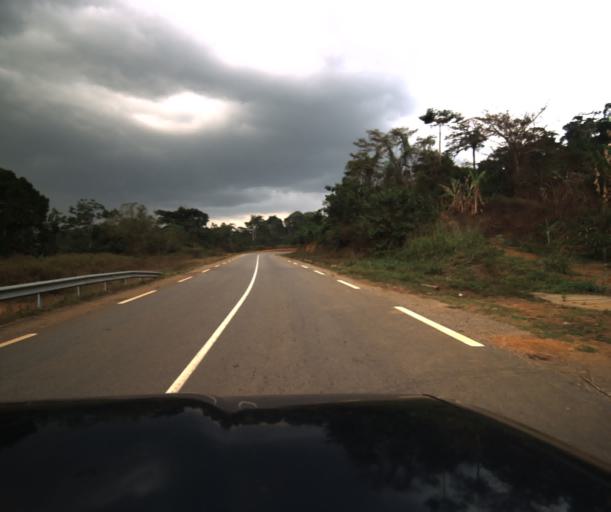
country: CM
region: Centre
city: Mbankomo
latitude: 3.6609
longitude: 11.3417
